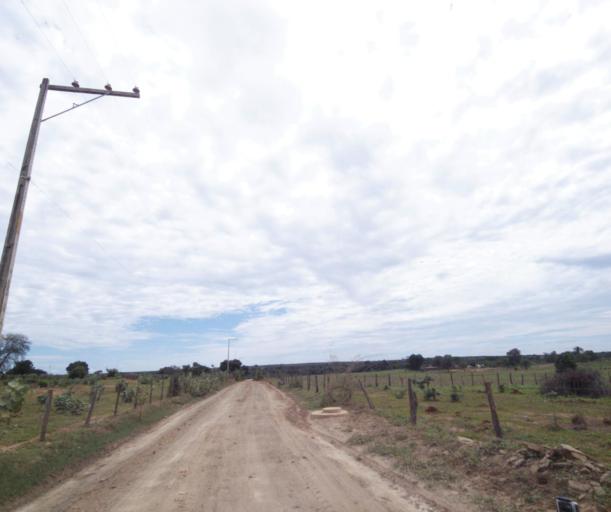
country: BR
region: Bahia
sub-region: Carinhanha
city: Carinhanha
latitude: -14.2192
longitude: -44.2907
